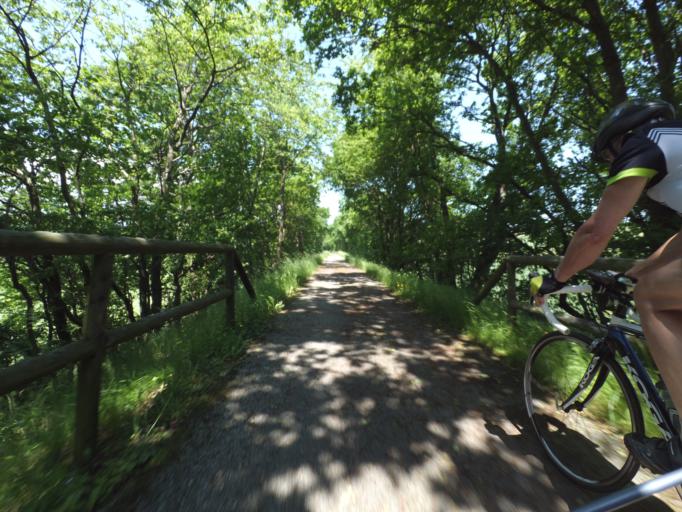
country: DE
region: Rheinland-Pfalz
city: Leiningen
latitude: 50.1223
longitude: 7.5698
